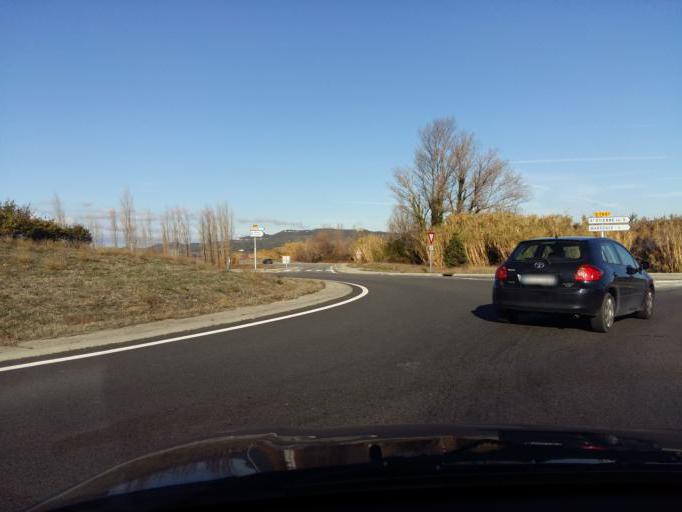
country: FR
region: Languedoc-Roussillon
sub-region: Departement du Gard
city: Orsan
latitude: 44.1329
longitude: 4.6735
